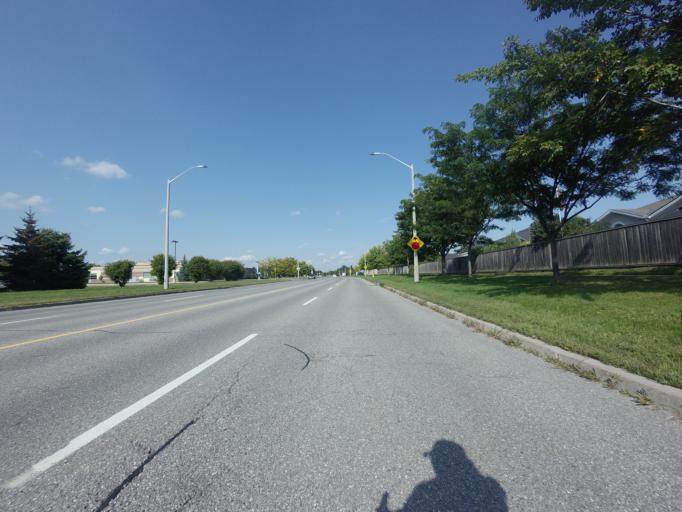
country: CA
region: Ontario
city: Ottawa
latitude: 45.2755
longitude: -75.6893
